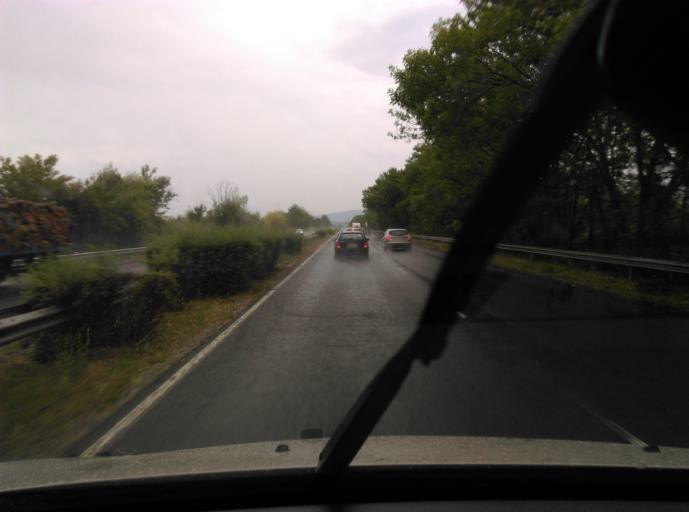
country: BG
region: Burgas
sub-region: Obshtina Burgas
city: Burgas
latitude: 42.4479
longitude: 27.4558
